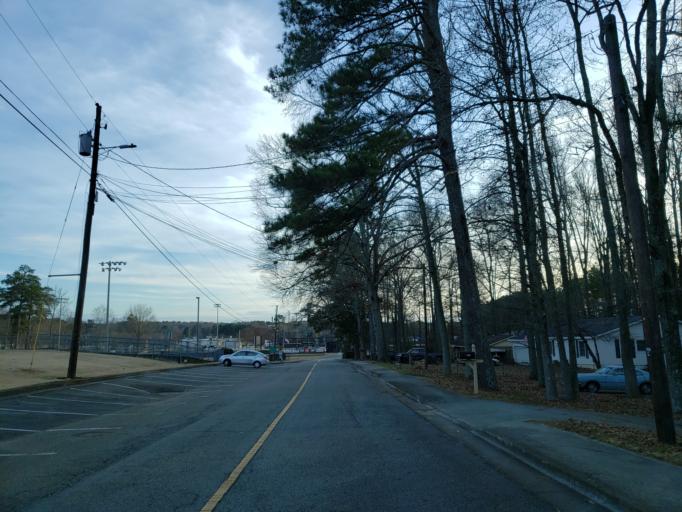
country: US
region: Georgia
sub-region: Cobb County
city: Kennesaw
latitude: 34.0249
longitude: -84.6220
